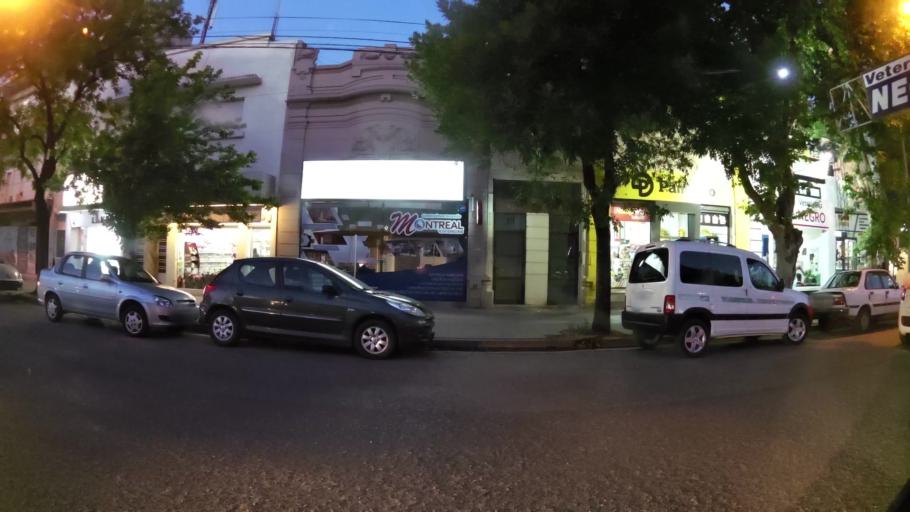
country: AR
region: Cordoba
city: Villa Maria
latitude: -32.4102
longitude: -63.2427
